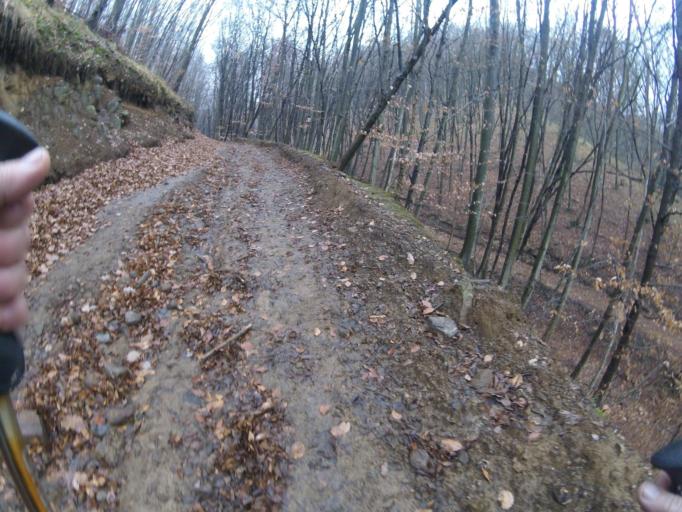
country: HU
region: Pest
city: Szob
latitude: 47.9210
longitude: 18.8859
